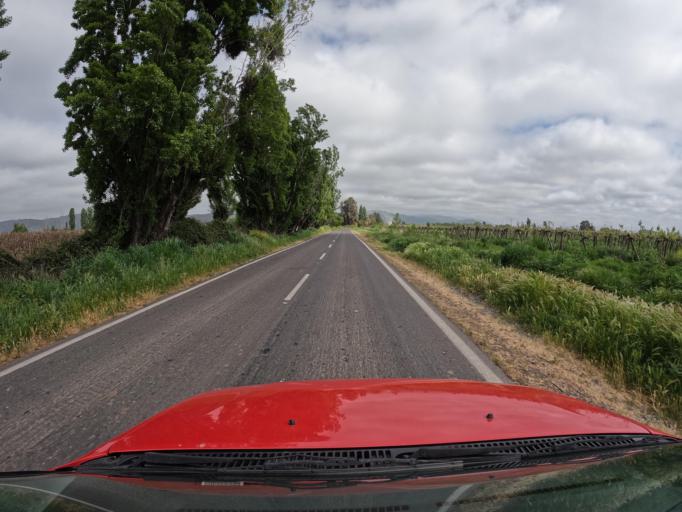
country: CL
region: O'Higgins
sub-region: Provincia de Colchagua
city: Santa Cruz
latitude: -34.6757
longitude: -71.3696
